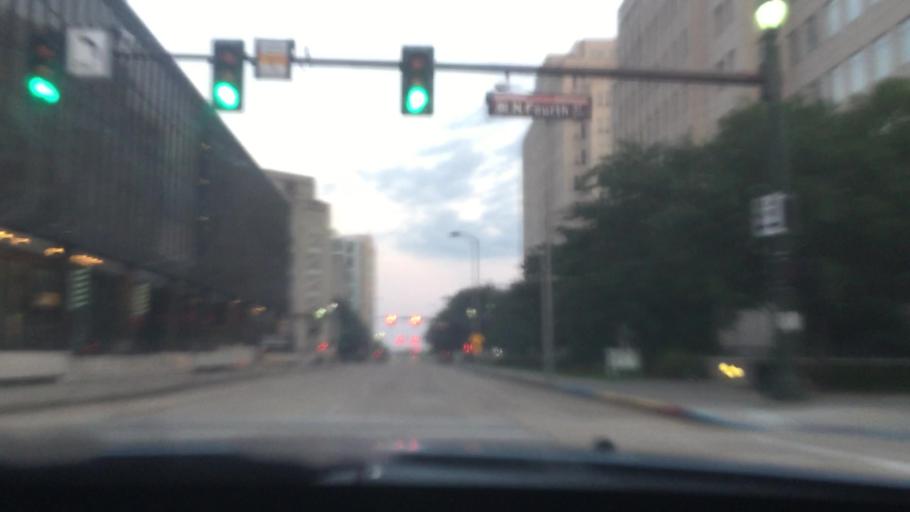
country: US
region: Louisiana
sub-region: West Baton Rouge Parish
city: Port Allen
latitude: 30.4526
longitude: -91.1872
